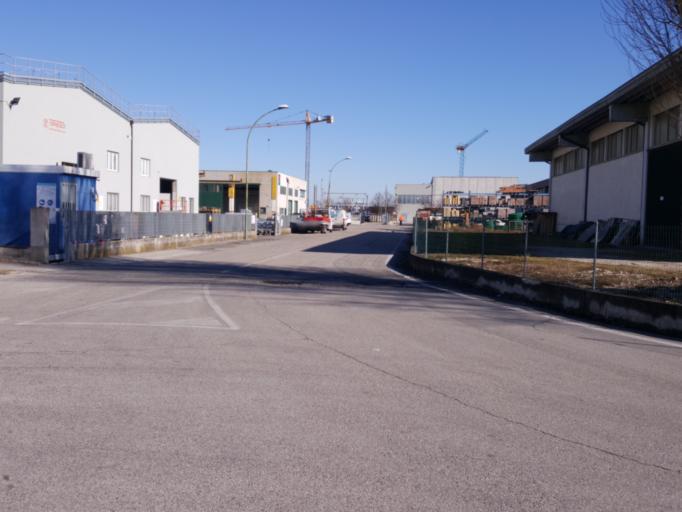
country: IT
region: Veneto
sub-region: Provincia di Venezia
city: Noventa di Piave
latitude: 45.6742
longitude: 12.5324
